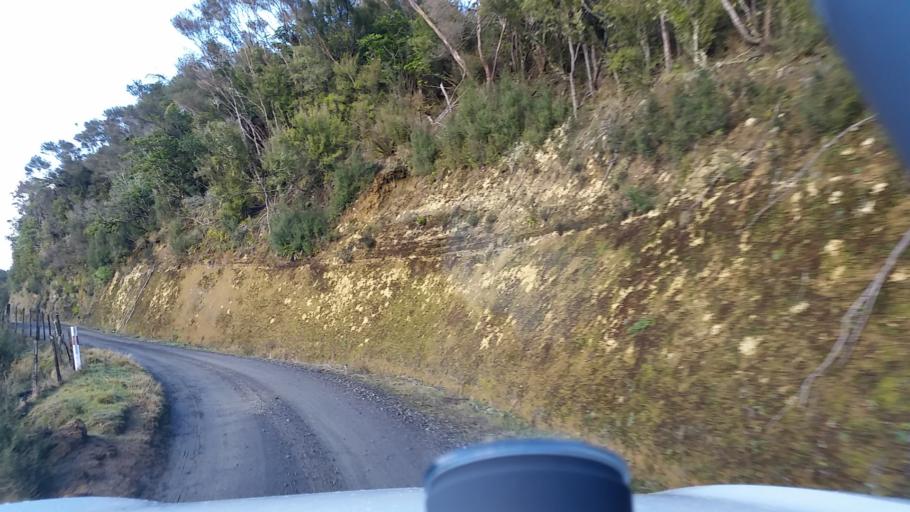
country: NZ
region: Taranaki
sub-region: South Taranaki District
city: Eltham
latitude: -39.4225
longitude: 174.5567
